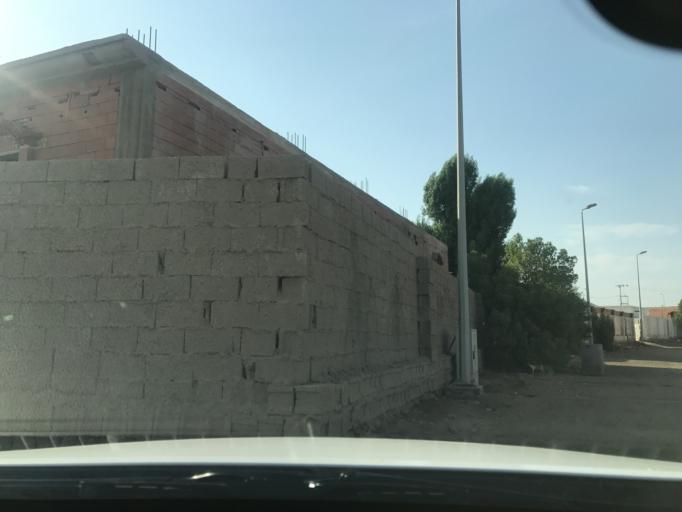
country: SA
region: Makkah
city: Al Jumum
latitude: 21.4496
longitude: 39.5345
